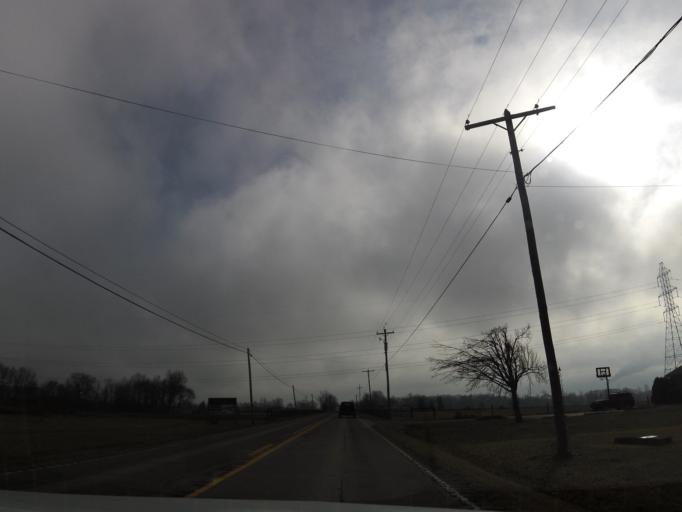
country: US
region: Indiana
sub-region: Jefferson County
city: North Madison
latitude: 38.7855
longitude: -85.4291
